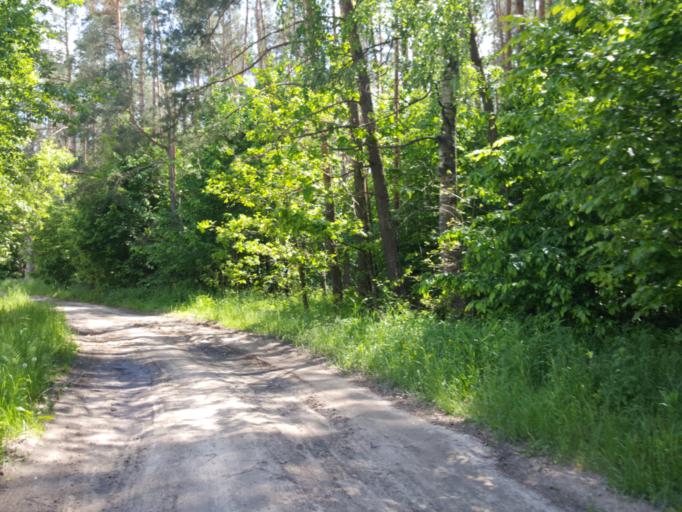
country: PL
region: Podlasie
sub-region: Powiat hajnowski
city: Hajnowka
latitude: 52.5796
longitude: 23.6200
